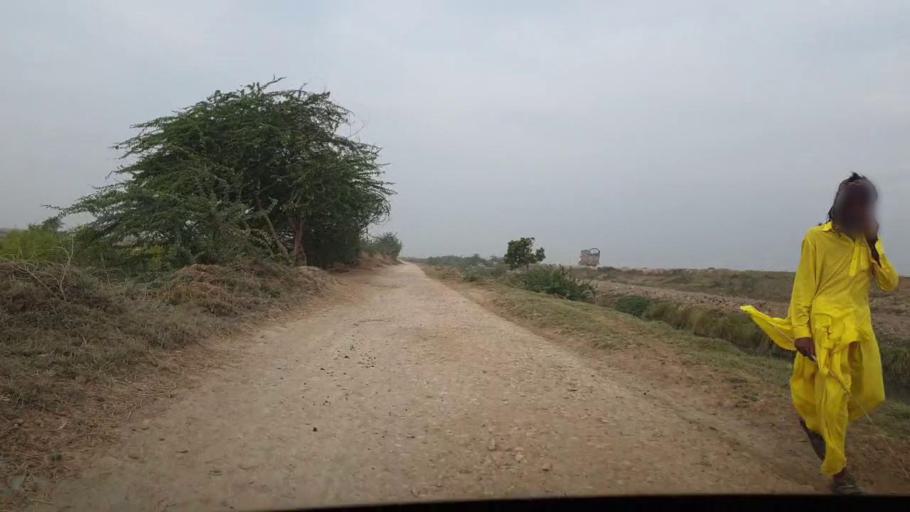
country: PK
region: Sindh
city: Chuhar Jamali
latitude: 24.4064
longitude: 67.9550
